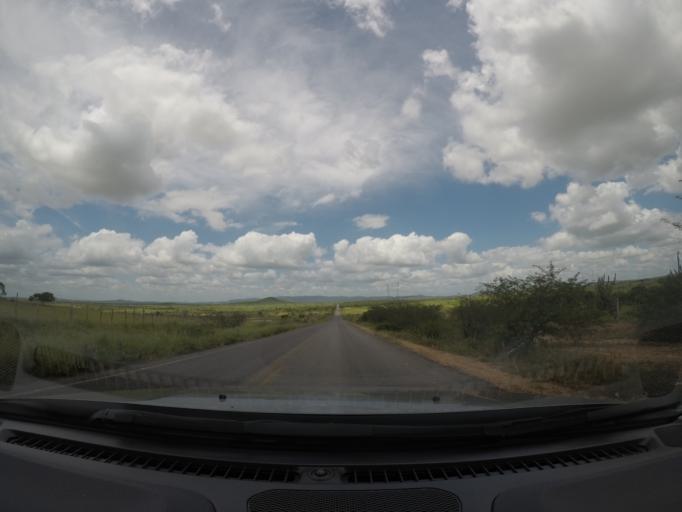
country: BR
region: Bahia
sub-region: Ipira
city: Ipira
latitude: -12.2514
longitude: -39.8140
